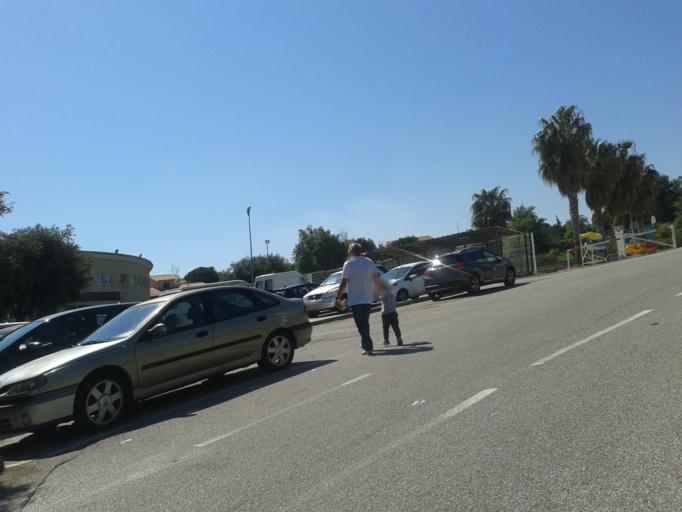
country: FR
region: Languedoc-Roussillon
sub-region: Departement des Pyrenees-Orientales
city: Perpignan
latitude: 42.6722
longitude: 2.8896
